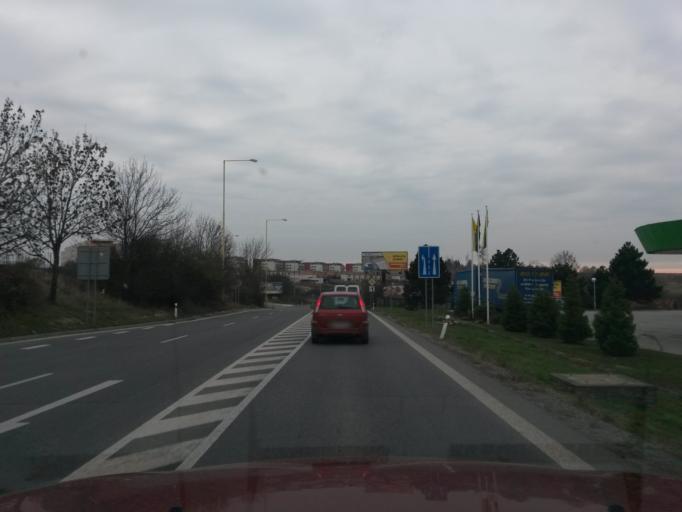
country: SK
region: Kosicky
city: Kosice
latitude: 48.7251
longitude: 21.2925
